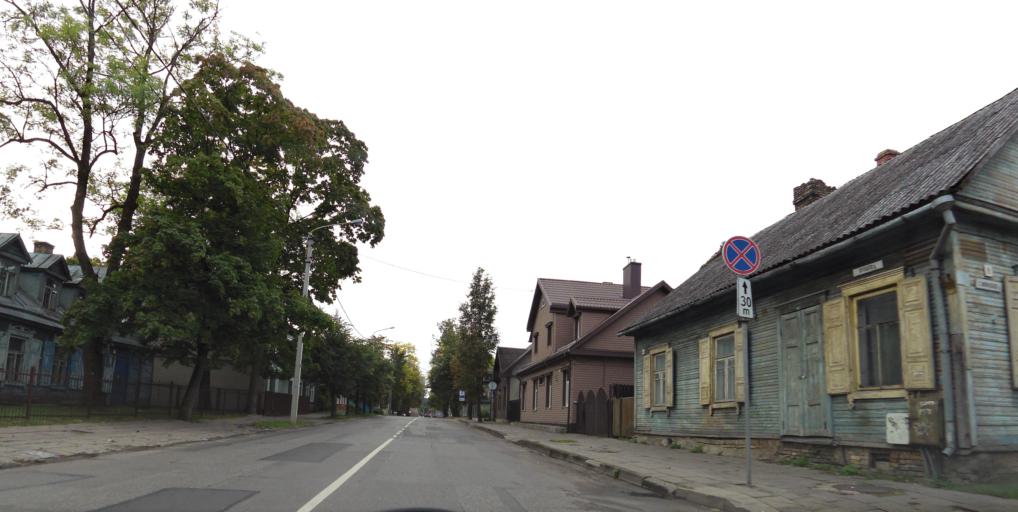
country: LT
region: Vilnius County
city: Seskine
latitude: 54.6938
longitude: 25.2560
